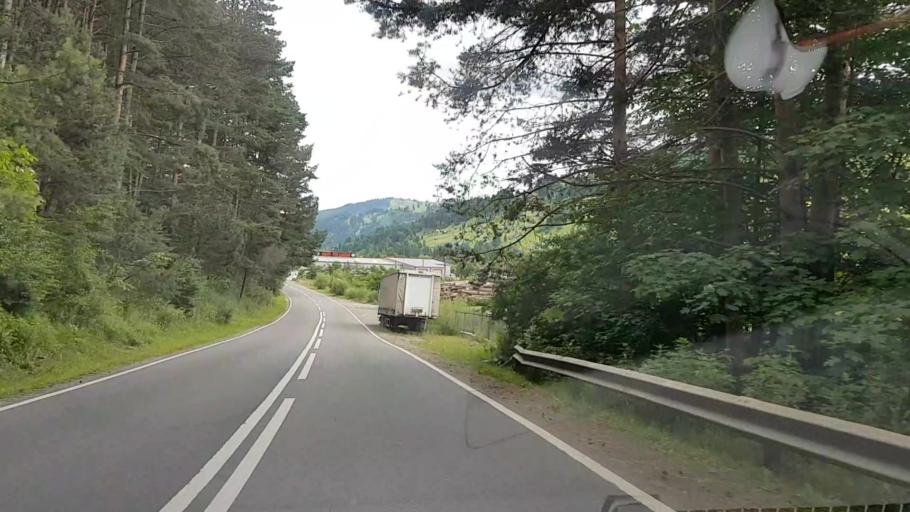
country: RO
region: Neamt
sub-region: Comuna Borca
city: Borca
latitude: 47.1718
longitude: 25.7947
